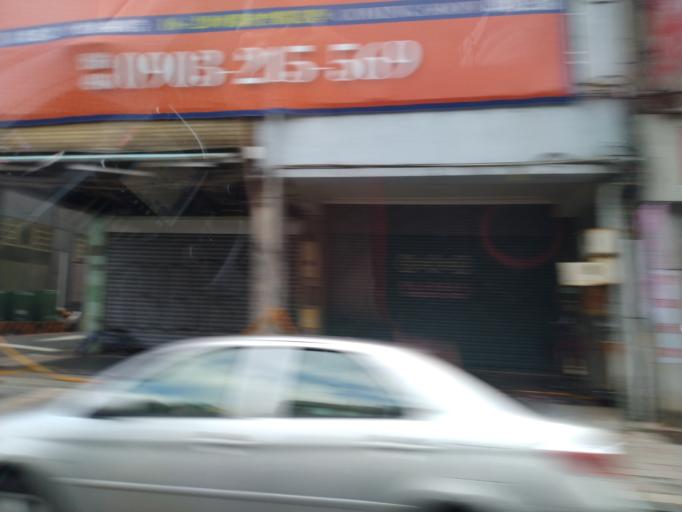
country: TW
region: Taipei
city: Taipei
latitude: 25.0686
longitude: 121.5153
